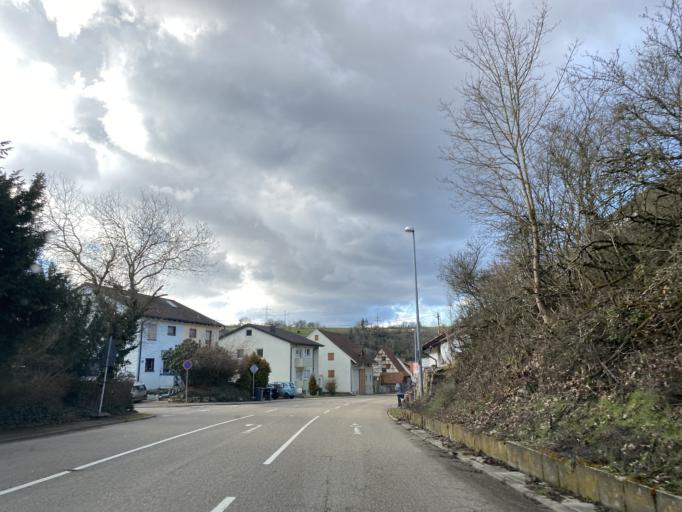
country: DE
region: Baden-Wuerttemberg
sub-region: Regierungsbezirk Stuttgart
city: Eberdingen
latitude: 48.8938
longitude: 8.9754
